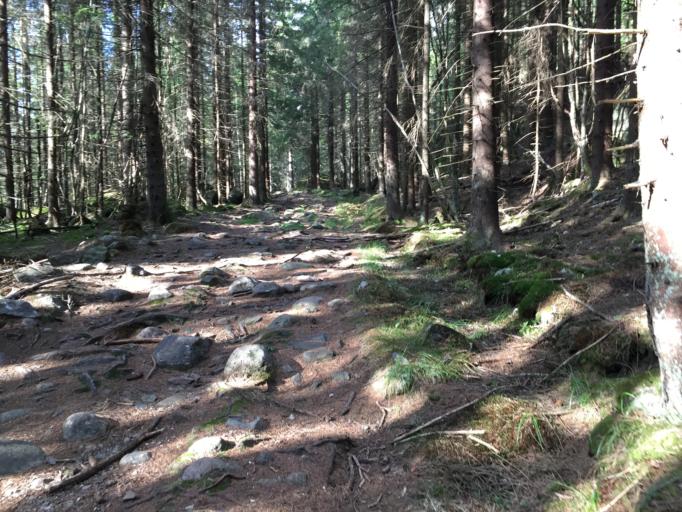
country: NO
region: Akershus
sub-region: Raelingen
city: Fjerdingby
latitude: 59.9130
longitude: 11.0288
